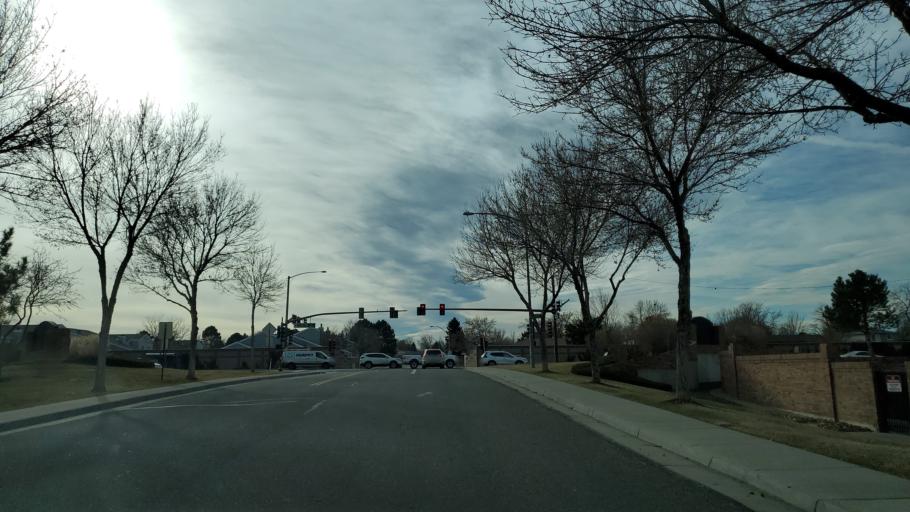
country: US
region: Colorado
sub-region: Adams County
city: Northglenn
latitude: 39.9146
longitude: -104.9457
